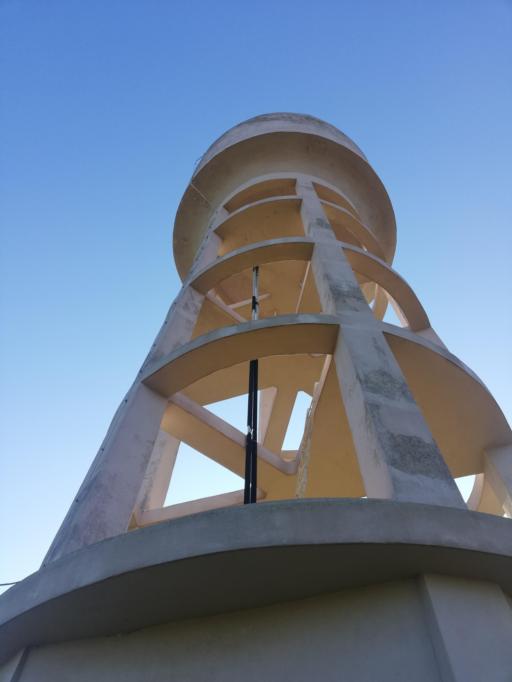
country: IT
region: Apulia
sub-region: Provincia di Bari
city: Poggiorsini
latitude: 40.8586
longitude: 16.3300
